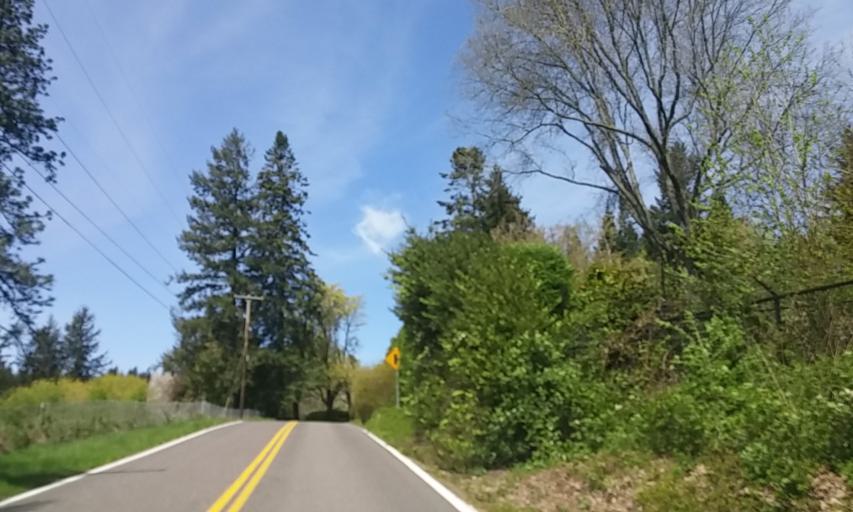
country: US
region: Oregon
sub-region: Washington County
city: West Slope
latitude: 45.5101
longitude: -122.7406
